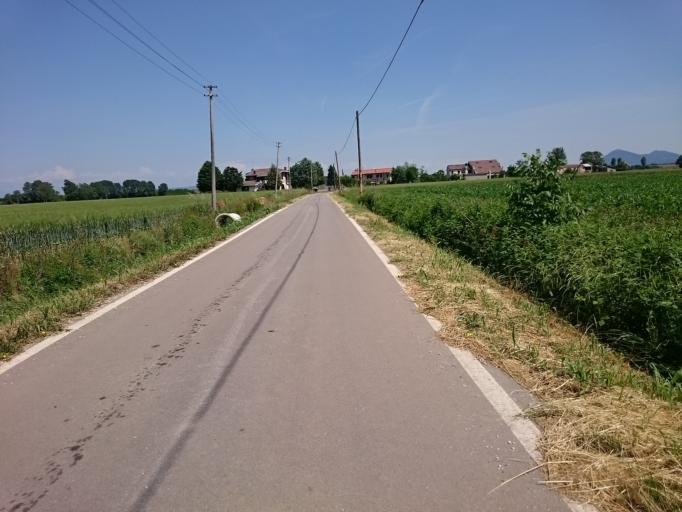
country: IT
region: Veneto
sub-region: Provincia di Padova
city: Saletto
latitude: 45.2514
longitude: 11.5597
